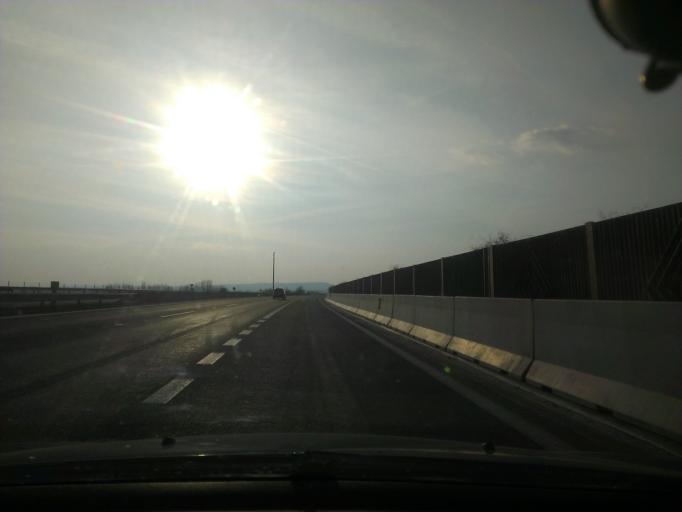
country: SK
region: Trnavsky
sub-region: Okres Trnava
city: Piestany
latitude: 48.6496
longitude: 17.8447
